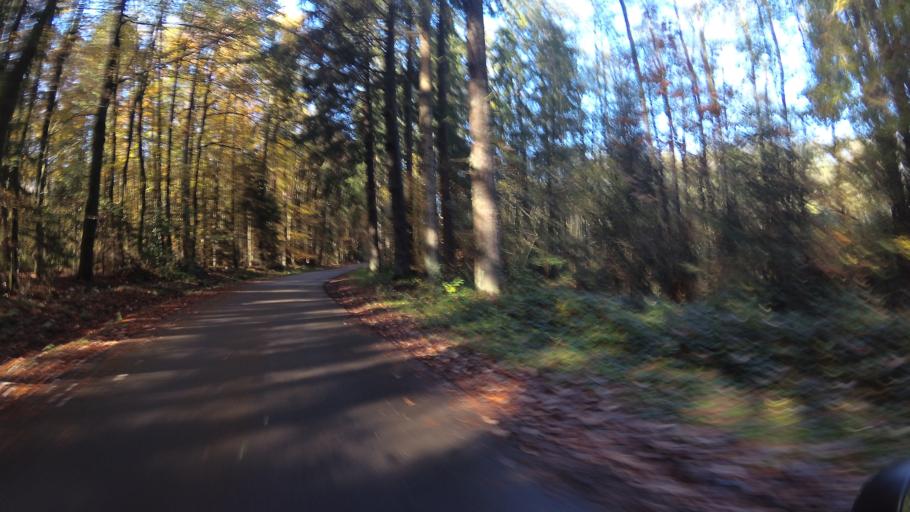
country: DE
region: Saarland
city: Losheim
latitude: 49.5389
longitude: 6.7724
